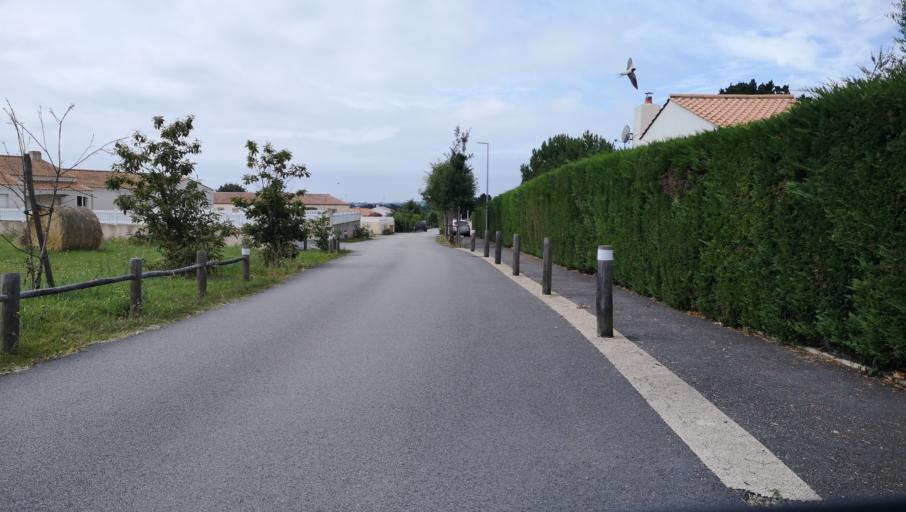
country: FR
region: Pays de la Loire
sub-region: Departement de la Vendee
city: Vaire
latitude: 46.5833
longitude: -1.7964
